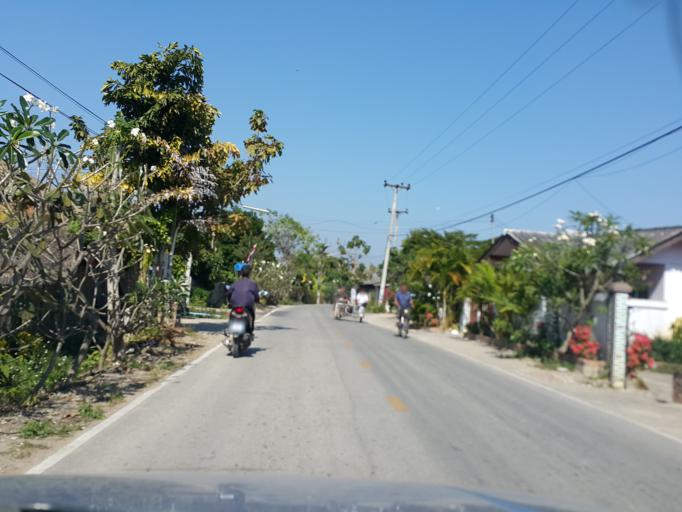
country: TH
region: Chiang Mai
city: Mae Wang
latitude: 18.5830
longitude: 98.7972
